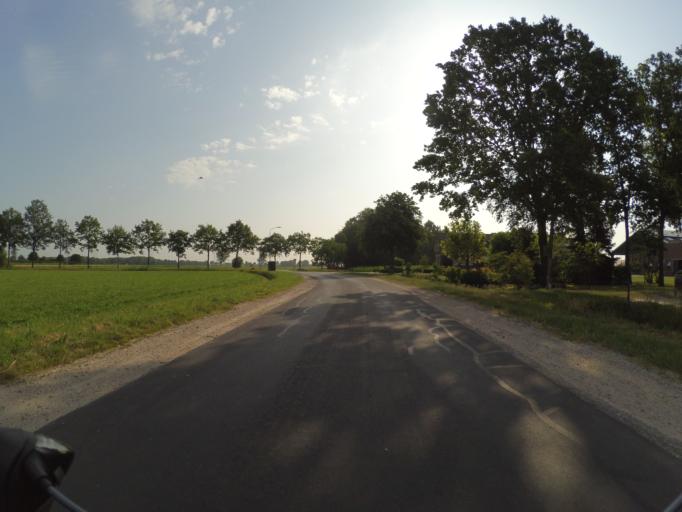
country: NL
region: North Brabant
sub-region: Gemeente Dongen
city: Dongen
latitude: 51.6250
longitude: 4.9876
